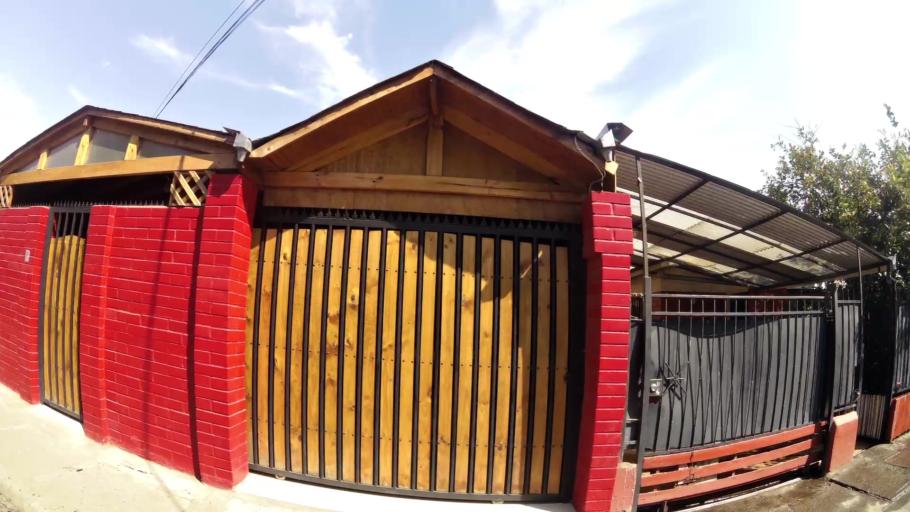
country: CL
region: Santiago Metropolitan
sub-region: Provincia de Santiago
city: La Pintana
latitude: -33.5624
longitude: -70.6504
